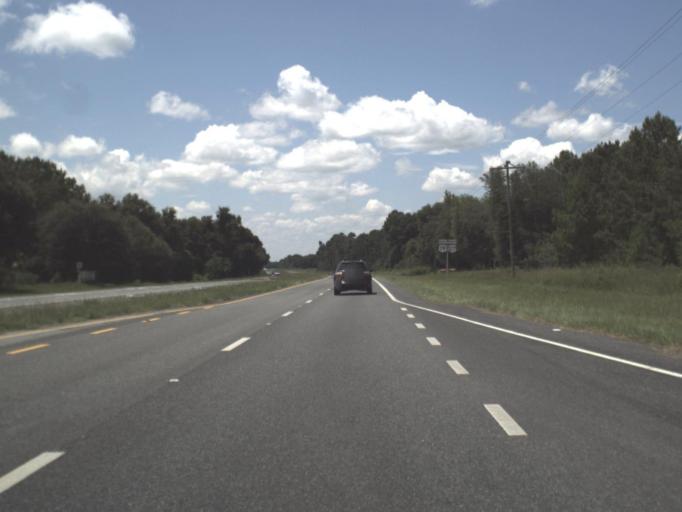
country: US
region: Florida
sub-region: Jefferson County
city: Monticello
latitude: 30.3202
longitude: -83.7633
